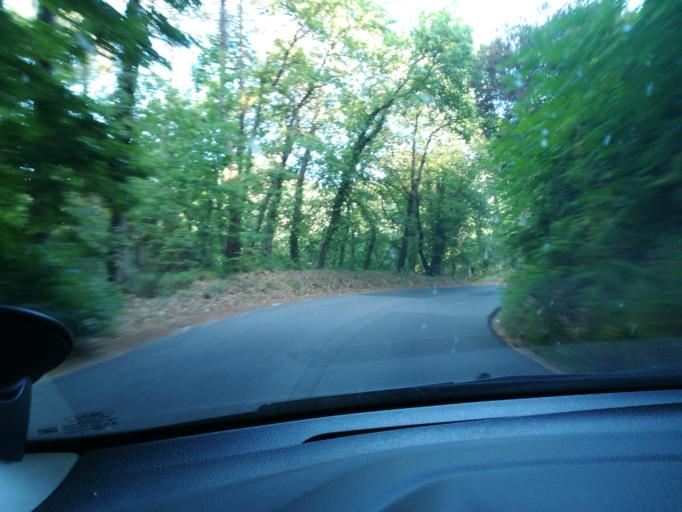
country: IT
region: Tuscany
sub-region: Provincia di Lucca
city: Stiava
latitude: 43.9155
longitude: 10.3400
